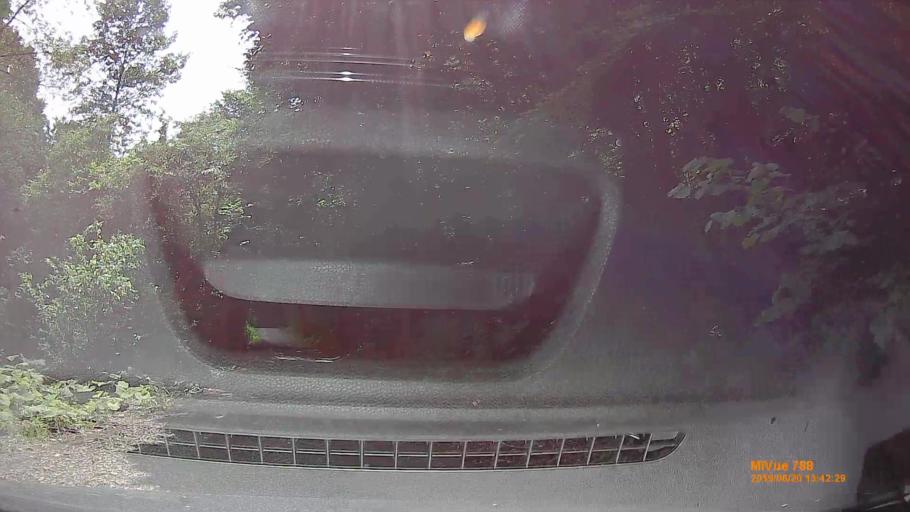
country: HU
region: Baranya
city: Hosszuheteny
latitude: 46.1843
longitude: 18.3532
